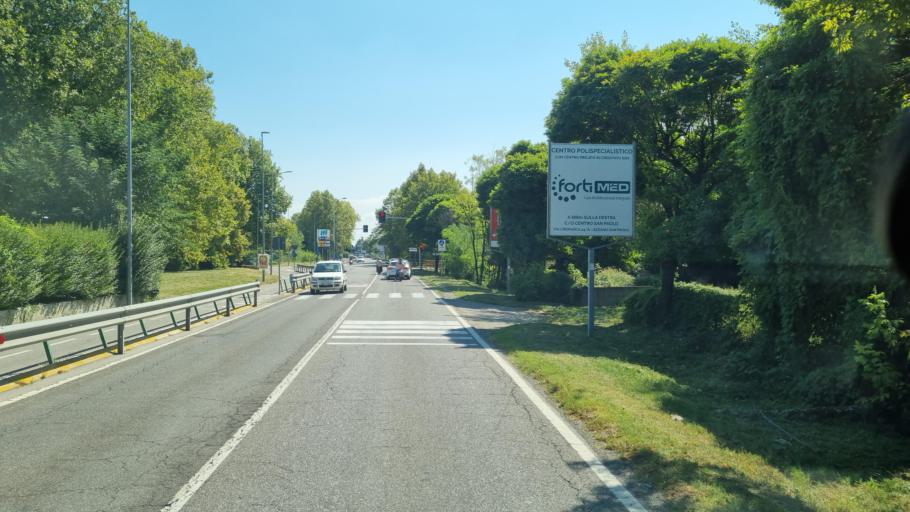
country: IT
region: Lombardy
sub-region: Provincia di Bergamo
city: Azzano San Paolo
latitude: 45.6664
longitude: 9.6765
